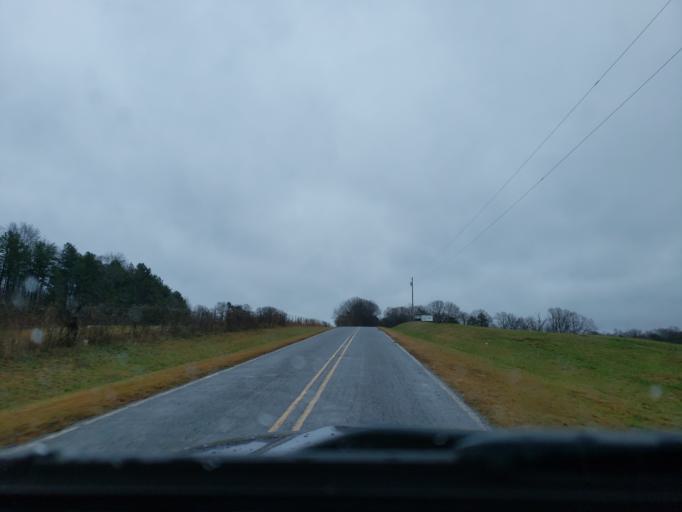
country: US
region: North Carolina
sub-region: Cleveland County
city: White Plains
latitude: 35.2026
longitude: -81.3635
